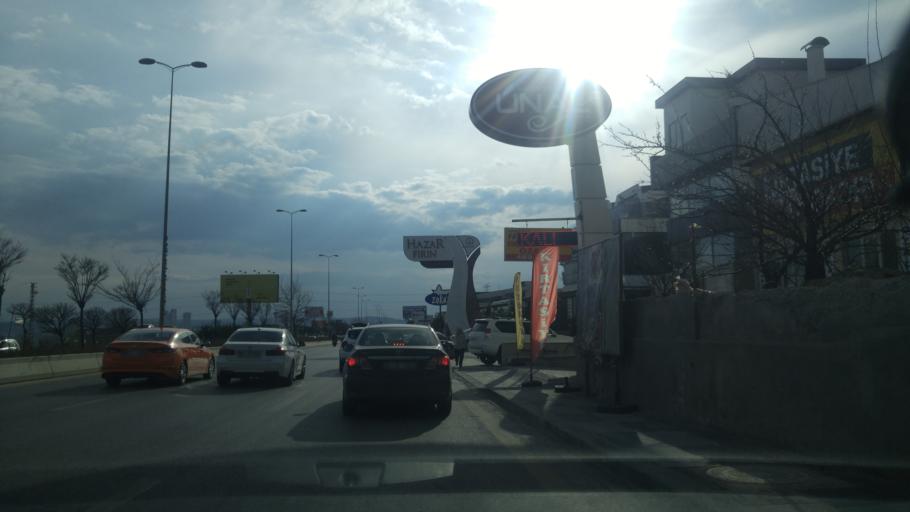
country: TR
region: Ankara
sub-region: Goelbasi
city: Golbasi
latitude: 39.8321
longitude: 32.7508
